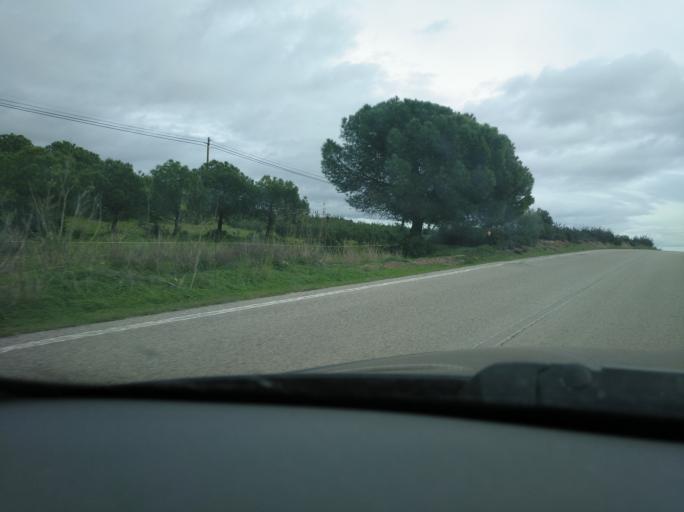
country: PT
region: Faro
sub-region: Castro Marim
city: Castro Marim
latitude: 37.2214
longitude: -7.4792
